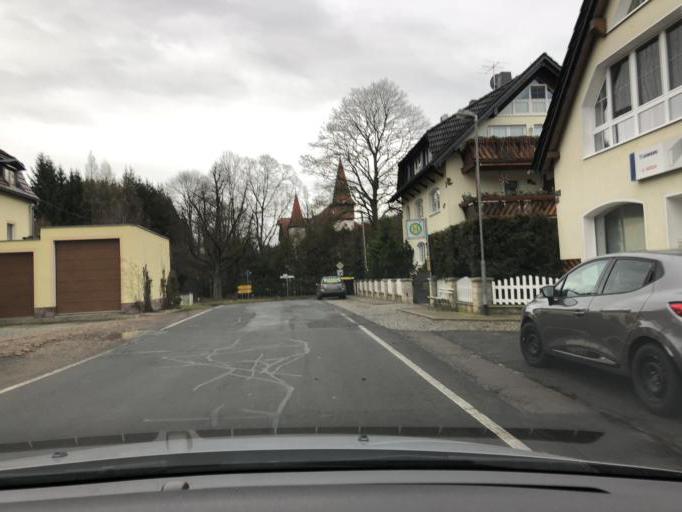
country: DE
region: Saxony
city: Rosswein
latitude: 51.0657
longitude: 13.2399
